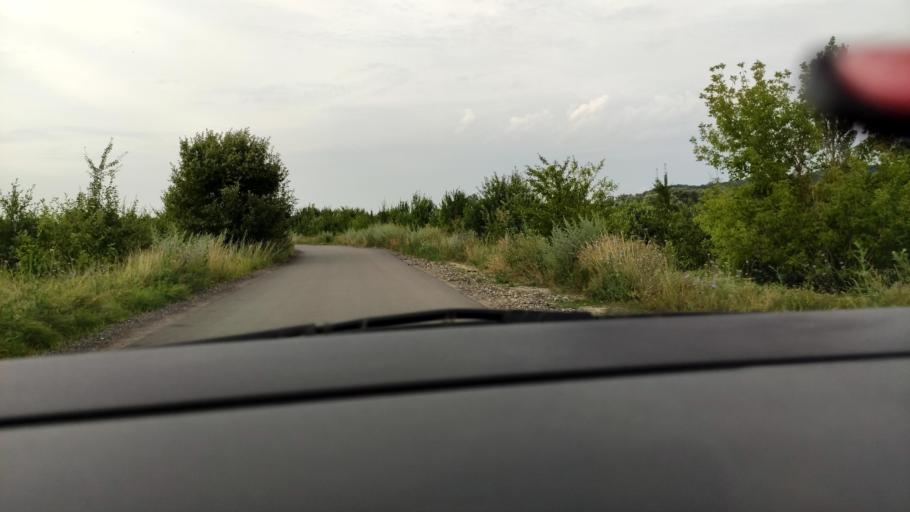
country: RU
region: Voronezj
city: Ramon'
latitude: 51.9000
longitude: 39.3501
